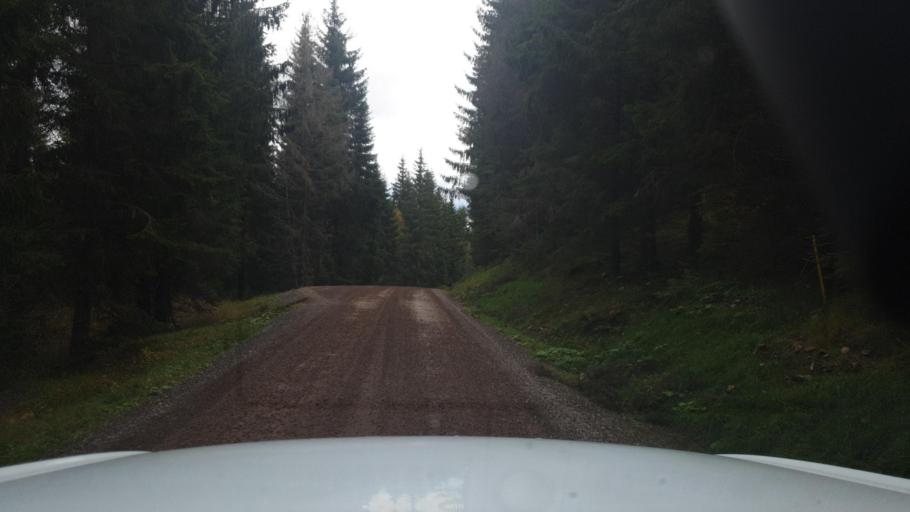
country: SE
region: Vaermland
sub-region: Eda Kommun
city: Charlottenberg
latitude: 60.0421
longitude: 12.5774
